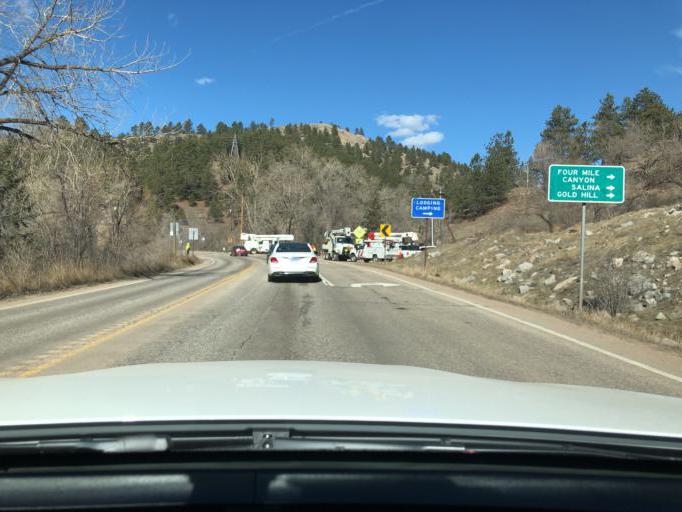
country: US
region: Colorado
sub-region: Boulder County
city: Boulder
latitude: 40.0150
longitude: -105.3232
